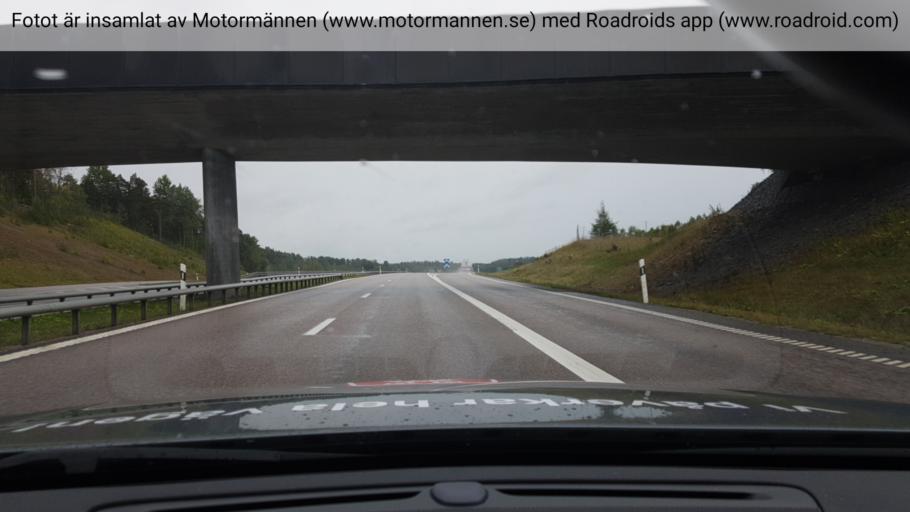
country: SE
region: Stockholm
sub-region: Nynashamns Kommun
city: Osmo
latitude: 58.9626
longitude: 17.9059
